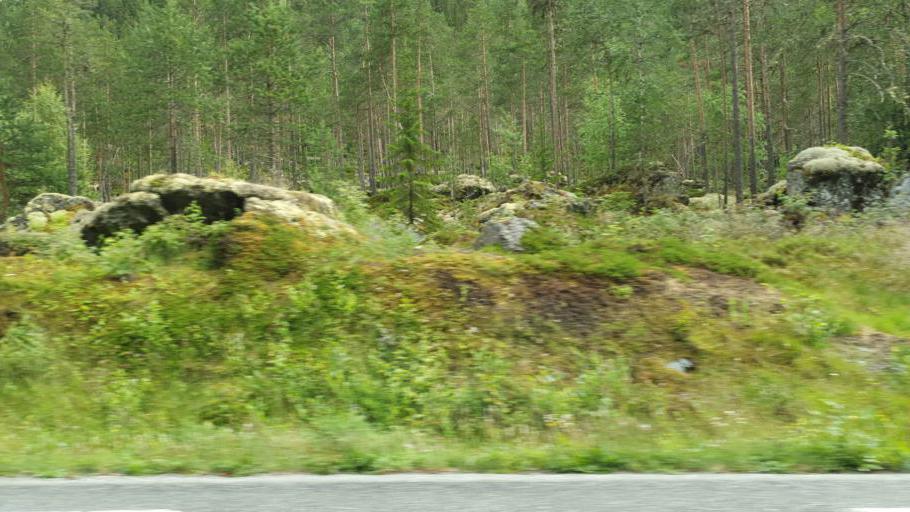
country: NO
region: Oppland
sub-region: Dovre
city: Dovre
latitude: 61.8475
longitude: 9.3205
